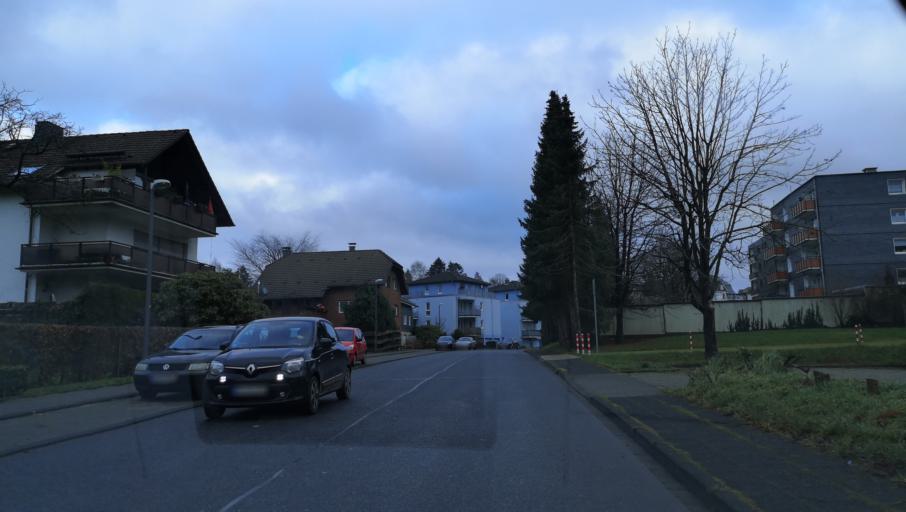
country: DE
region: North Rhine-Westphalia
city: Radevormwald
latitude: 51.1993
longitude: 7.3548
